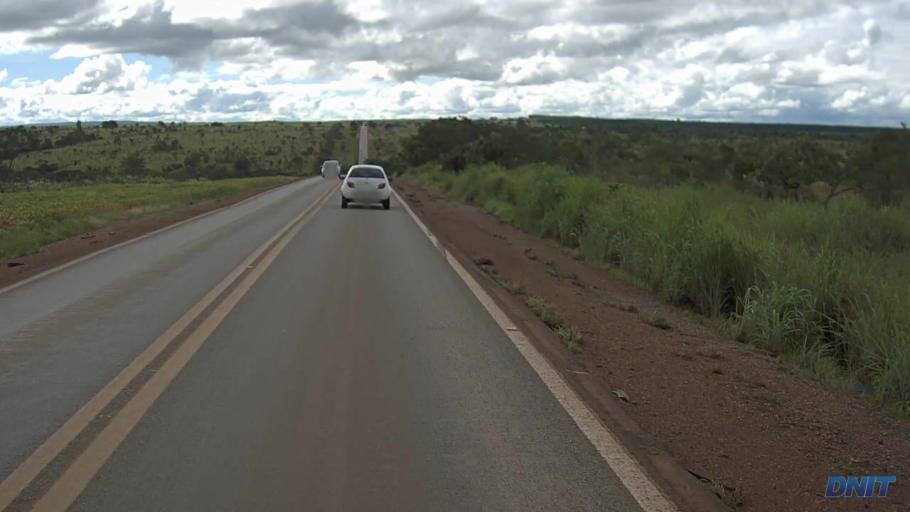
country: BR
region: Goias
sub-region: Padre Bernardo
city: Padre Bernardo
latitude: -15.2999
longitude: -48.2337
